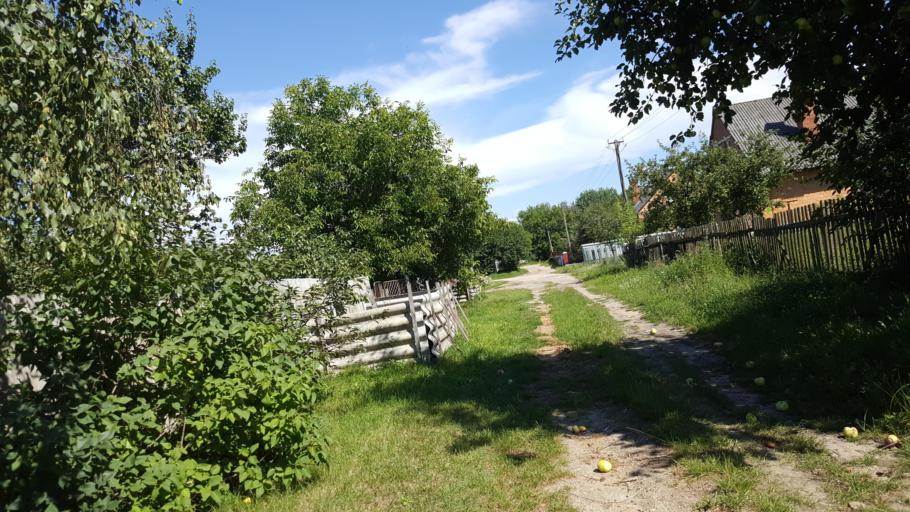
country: BY
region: Brest
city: Charnawchytsy
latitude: 52.2681
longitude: 23.5933
